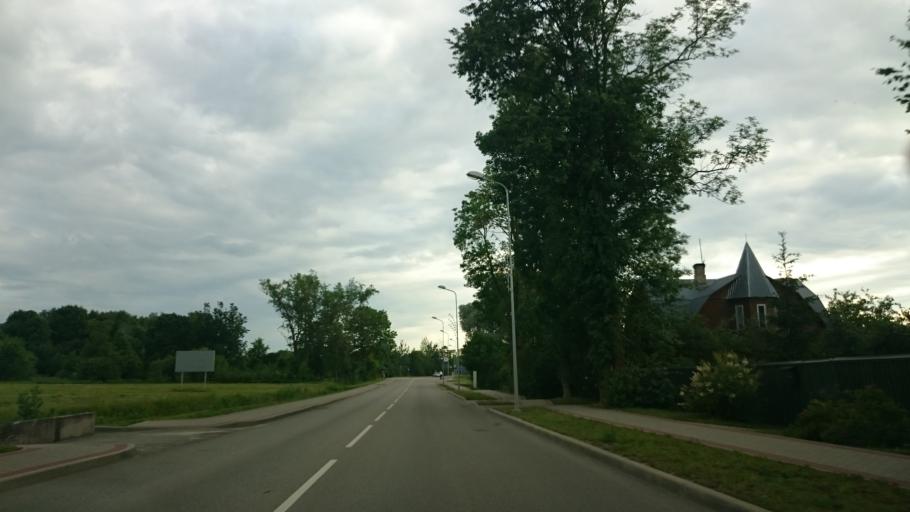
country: LV
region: Ludzas Rajons
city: Ludza
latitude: 56.5390
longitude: 27.7011
